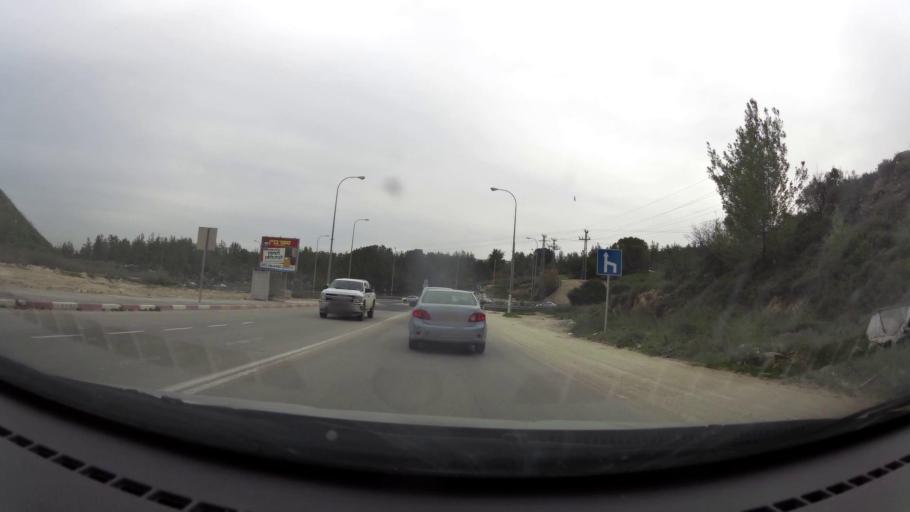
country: IL
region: Jerusalem
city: Bet Shemesh
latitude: 31.7051
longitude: 35.0082
